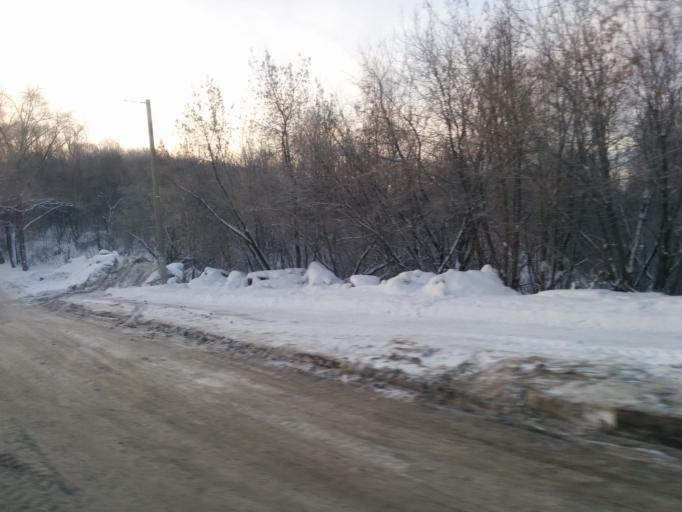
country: RU
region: Perm
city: Perm
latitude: 57.9968
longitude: 56.2776
